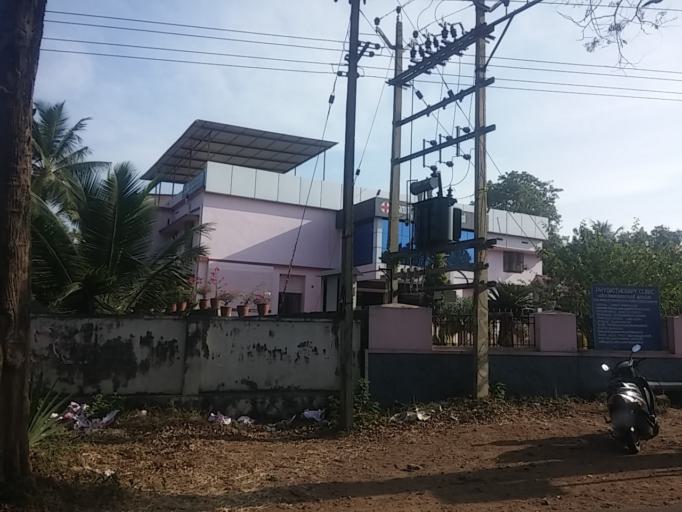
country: IN
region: Kerala
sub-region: Thrissur District
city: Chelakara
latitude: 10.5951
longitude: 76.5024
